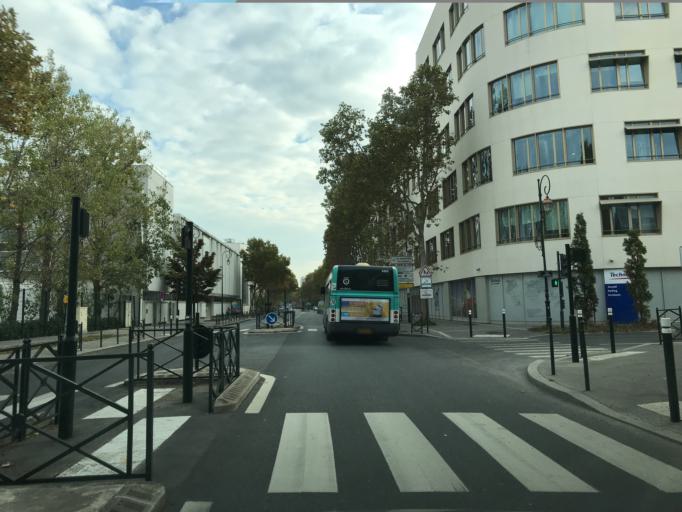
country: FR
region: Ile-de-France
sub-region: Departement des Hauts-de-Seine
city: La Defense
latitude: 48.9036
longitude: 2.2299
